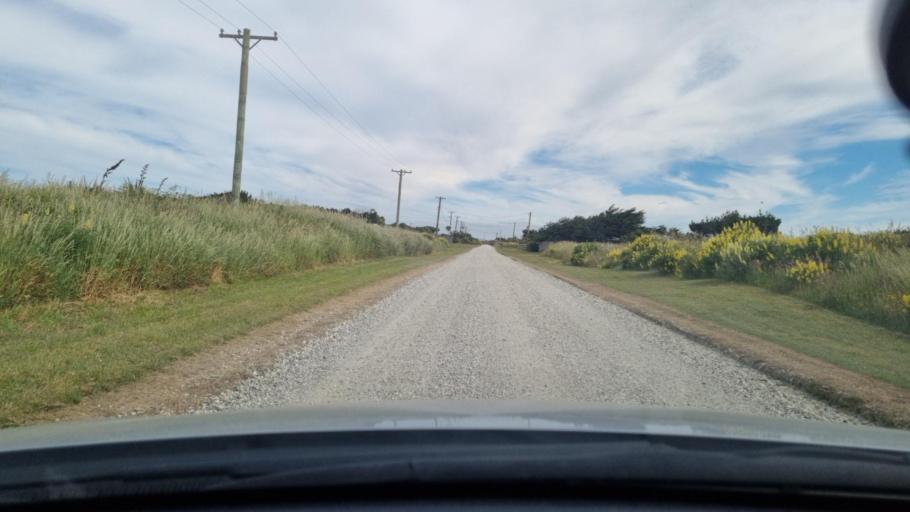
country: NZ
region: Southland
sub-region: Invercargill City
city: Invercargill
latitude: -46.4327
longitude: 168.2341
